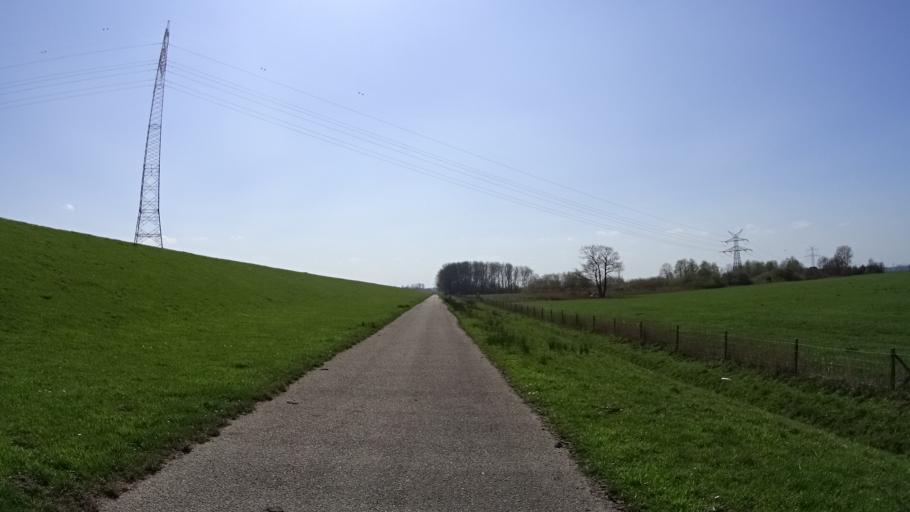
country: DE
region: Lower Saxony
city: Weener
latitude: 53.1494
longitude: 7.3706
